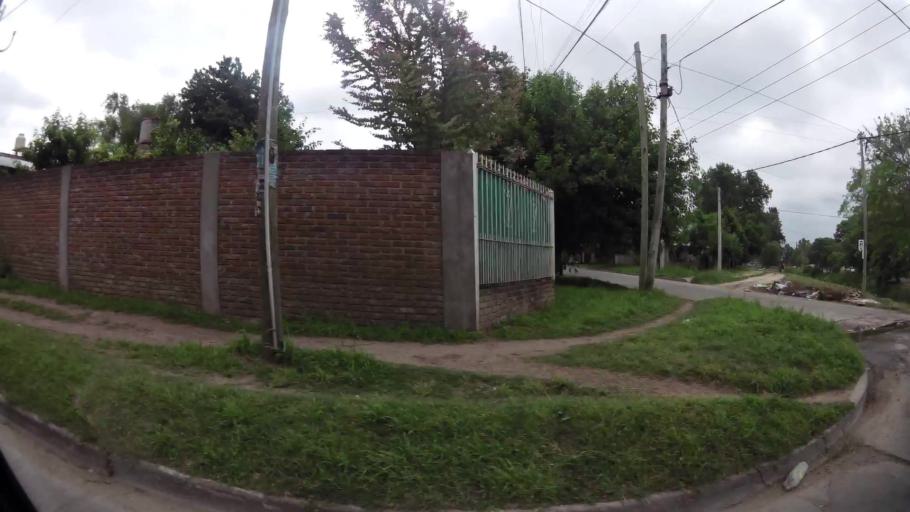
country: AR
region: Buenos Aires
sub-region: Partido de Ezeiza
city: Ezeiza
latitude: -34.8483
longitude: -58.5208
